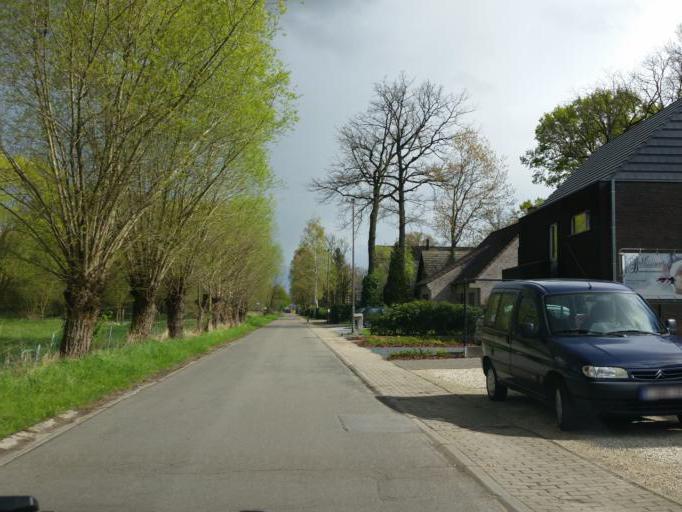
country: BE
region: Flanders
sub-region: Provincie Vlaams-Brabant
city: Boortmeerbeek
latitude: 50.9779
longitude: 4.5400
